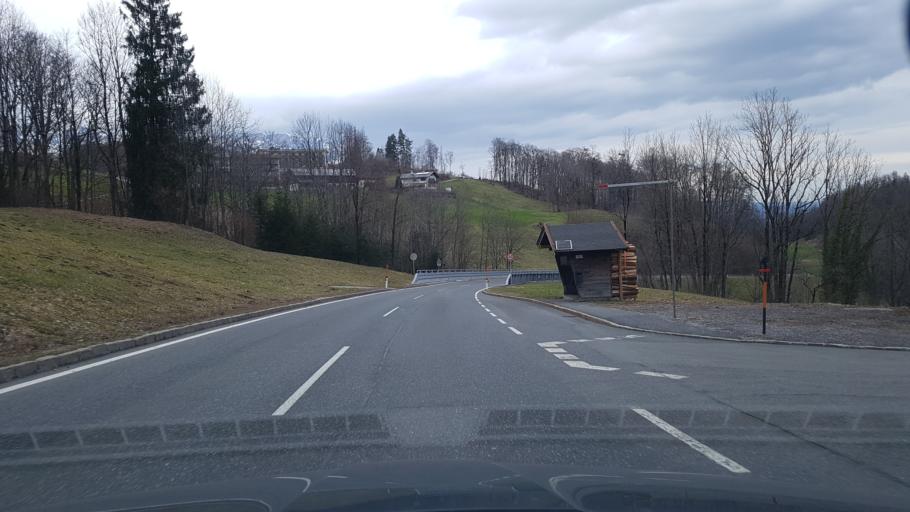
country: AT
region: Salzburg
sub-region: Politischer Bezirk Hallein
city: Hallein
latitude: 47.6621
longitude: 13.0948
